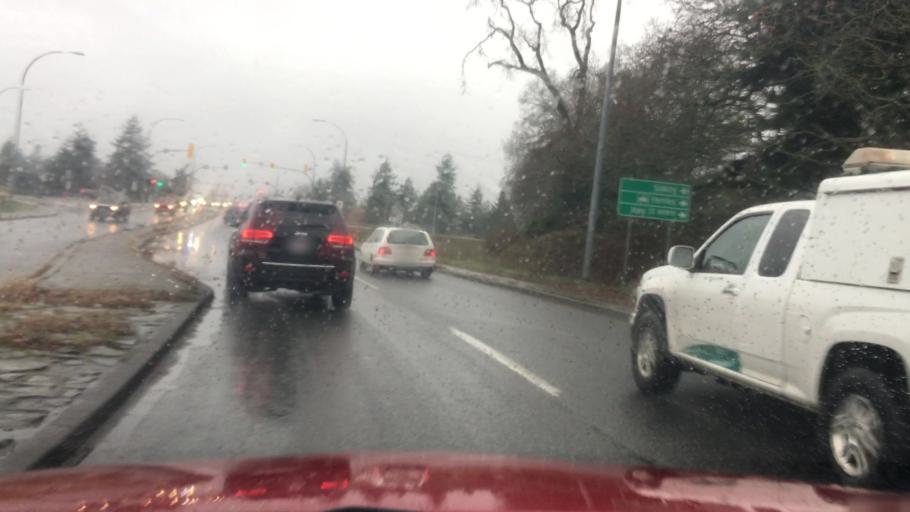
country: CA
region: British Columbia
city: Victoria
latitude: 48.4987
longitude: -123.3827
